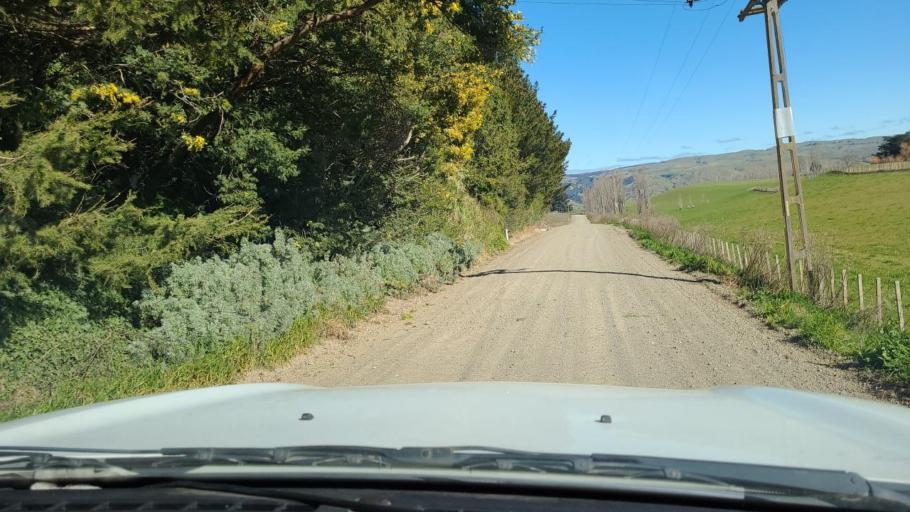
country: NZ
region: Hawke's Bay
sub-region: Napier City
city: Taradale
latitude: -39.4936
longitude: 176.4902
